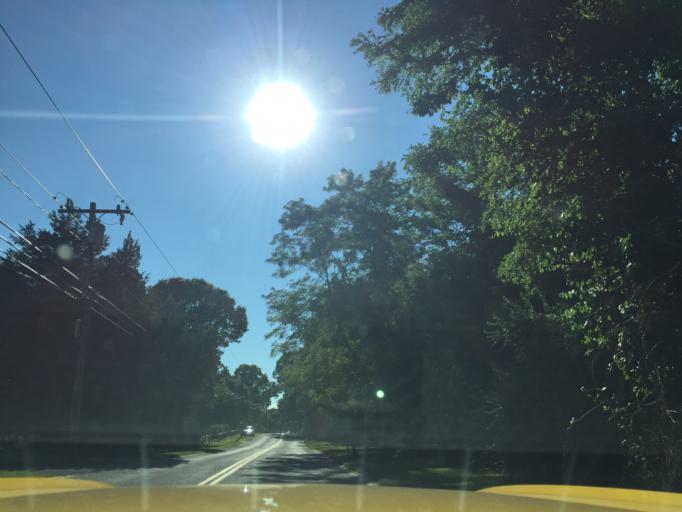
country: US
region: New York
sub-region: Suffolk County
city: Southold
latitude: 41.0428
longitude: -72.4071
